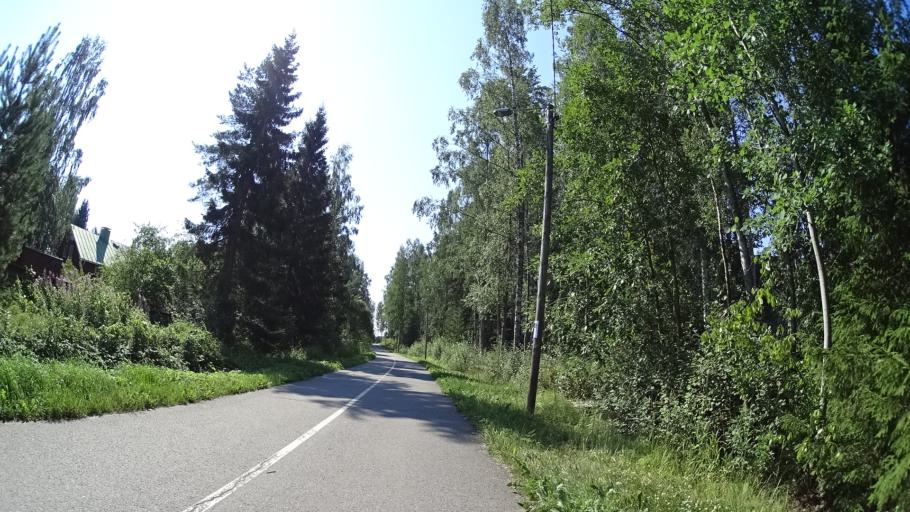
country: FI
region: Uusimaa
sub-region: Helsinki
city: Kerava
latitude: 60.3883
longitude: 25.0936
